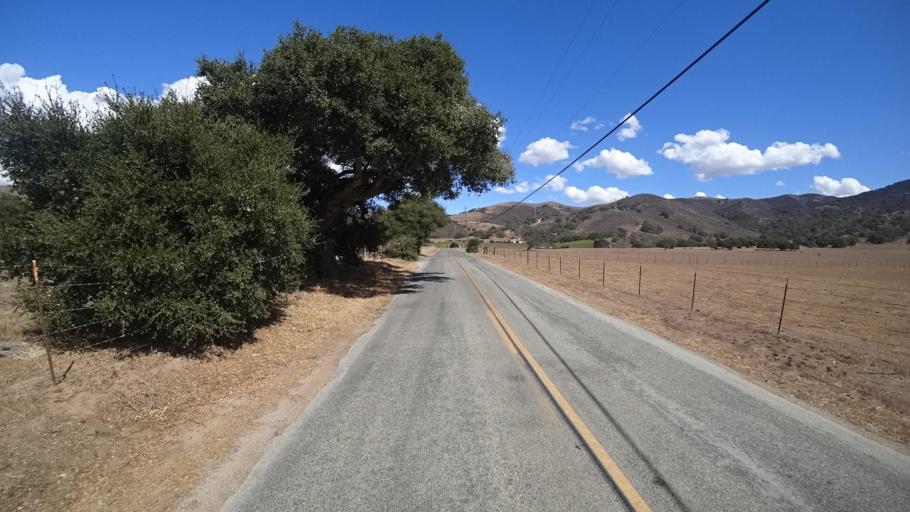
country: US
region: California
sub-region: Monterey County
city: Chualar
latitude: 36.5941
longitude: -121.4420
